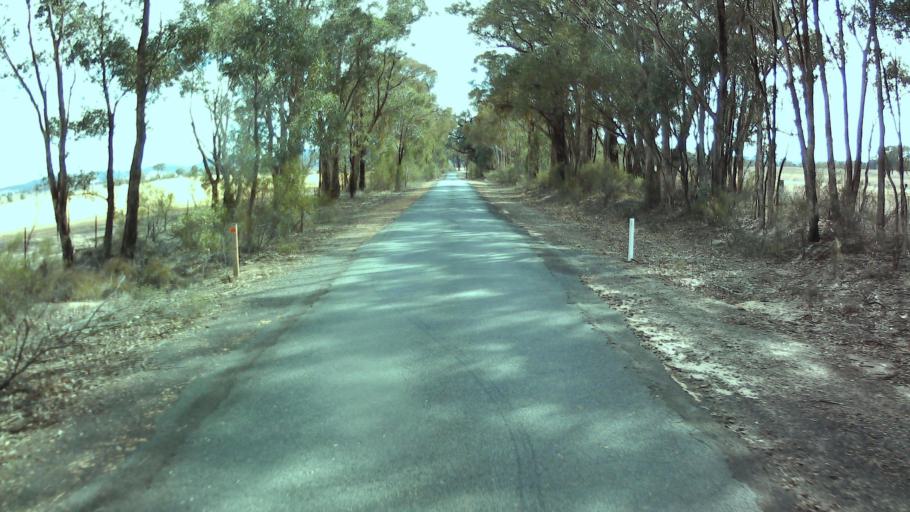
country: AU
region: New South Wales
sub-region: Weddin
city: Grenfell
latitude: -33.8529
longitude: 148.2191
